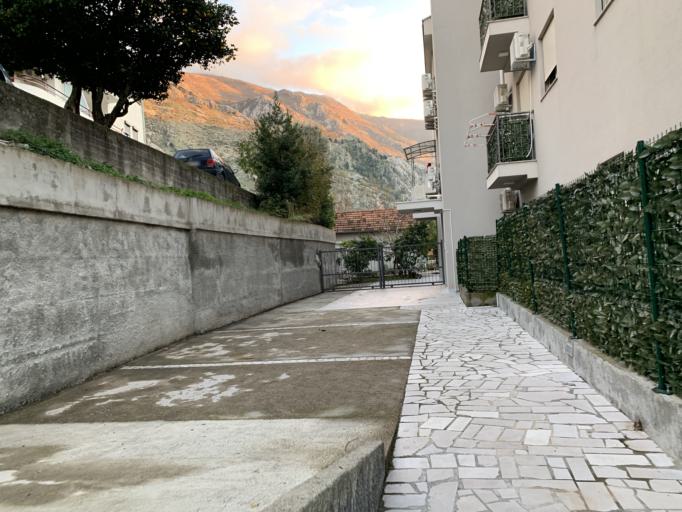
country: ME
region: Kotor
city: Kotor
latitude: 42.4306
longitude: 18.7699
